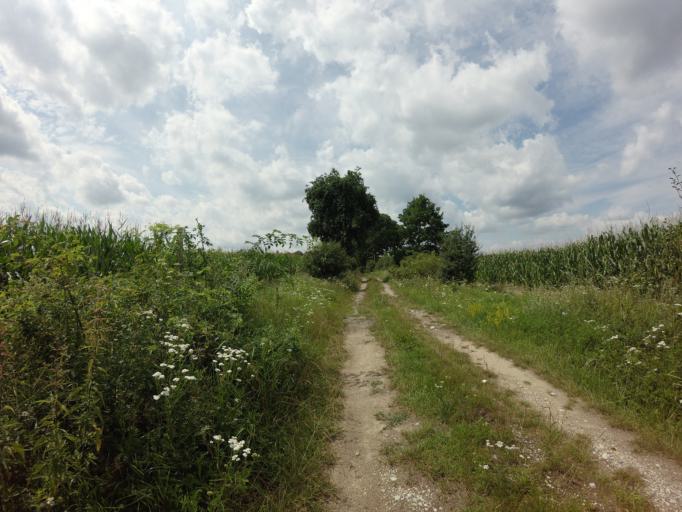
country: PL
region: Kujawsko-Pomorskie
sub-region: Powiat bydgoski
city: Koronowo
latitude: 53.3772
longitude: 18.0023
